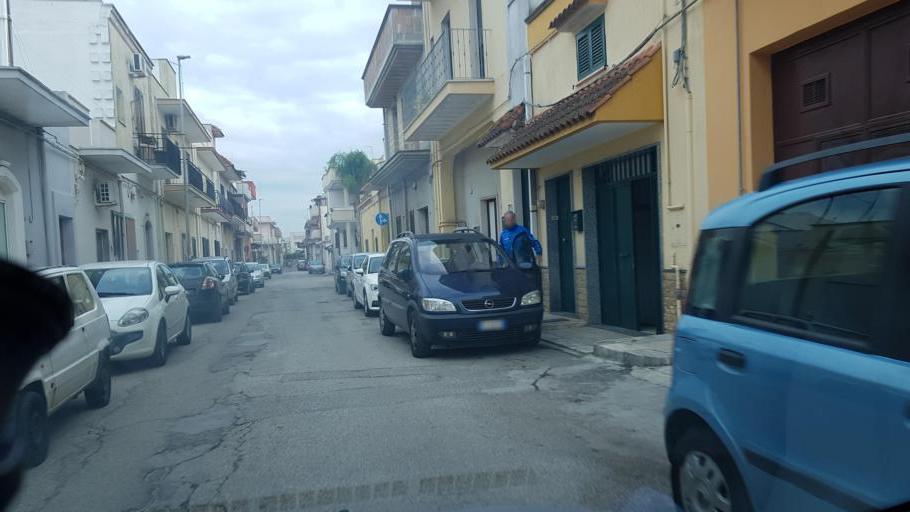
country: IT
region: Apulia
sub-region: Provincia di Brindisi
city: Oria
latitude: 40.5035
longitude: 17.6418
